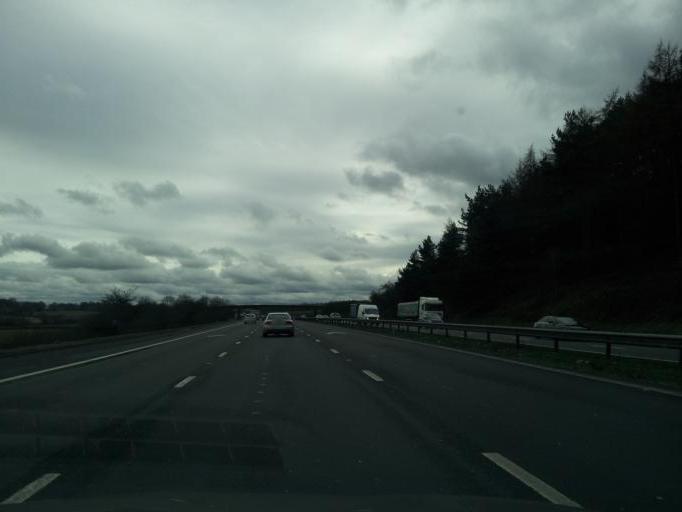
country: GB
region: England
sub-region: Staffordshire
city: Barlaston
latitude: 52.9377
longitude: -2.2150
